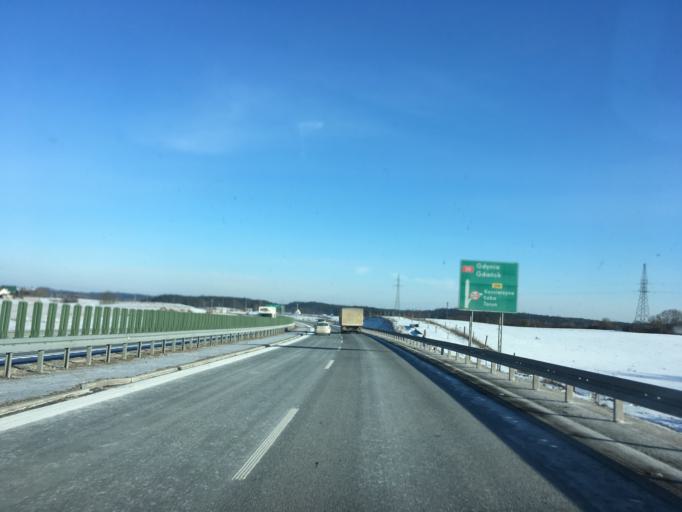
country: PL
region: Pomeranian Voivodeship
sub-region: Powiat koscierski
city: Koscierzyna
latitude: 54.1075
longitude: 17.9649
